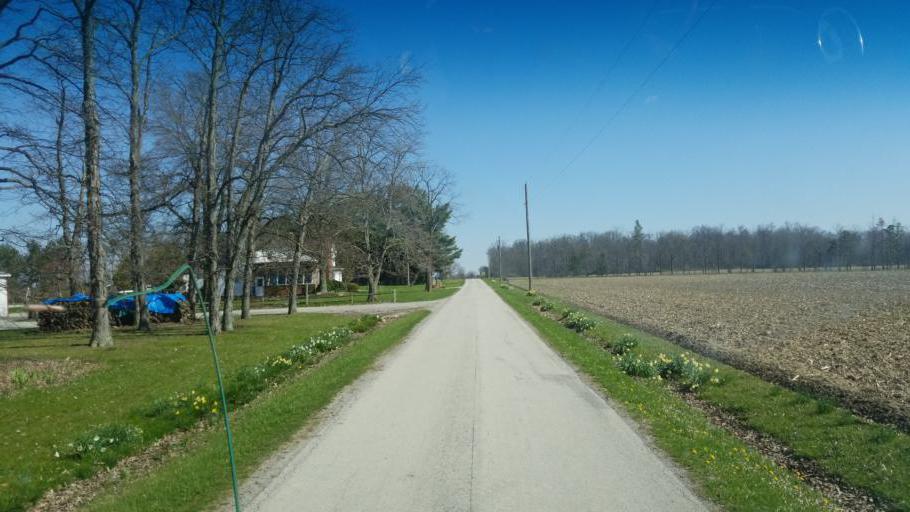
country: US
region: Ohio
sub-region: Wyandot County
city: Upper Sandusky
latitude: 40.7606
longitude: -83.3043
